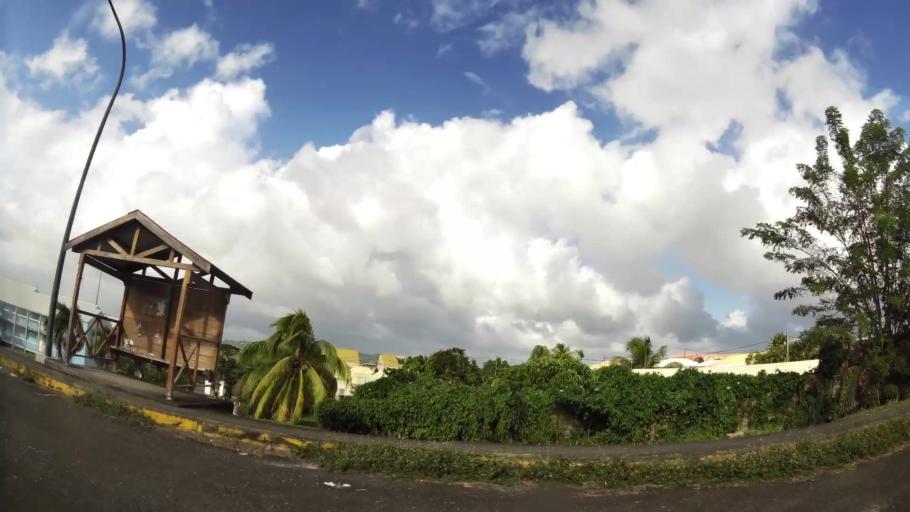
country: MQ
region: Martinique
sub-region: Martinique
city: Saint-Esprit
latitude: 14.5232
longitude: -60.9717
